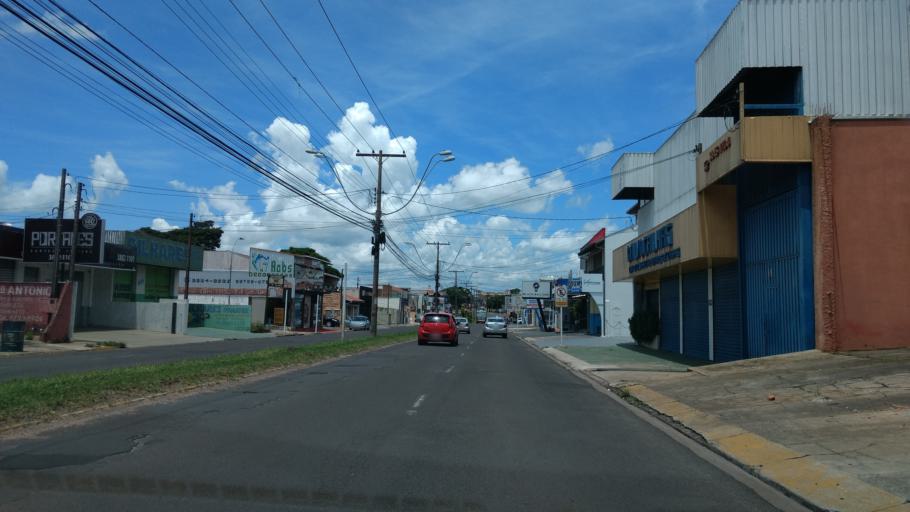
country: BR
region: Sao Paulo
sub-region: Botucatu
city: Botucatu
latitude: -22.8691
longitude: -48.4640
